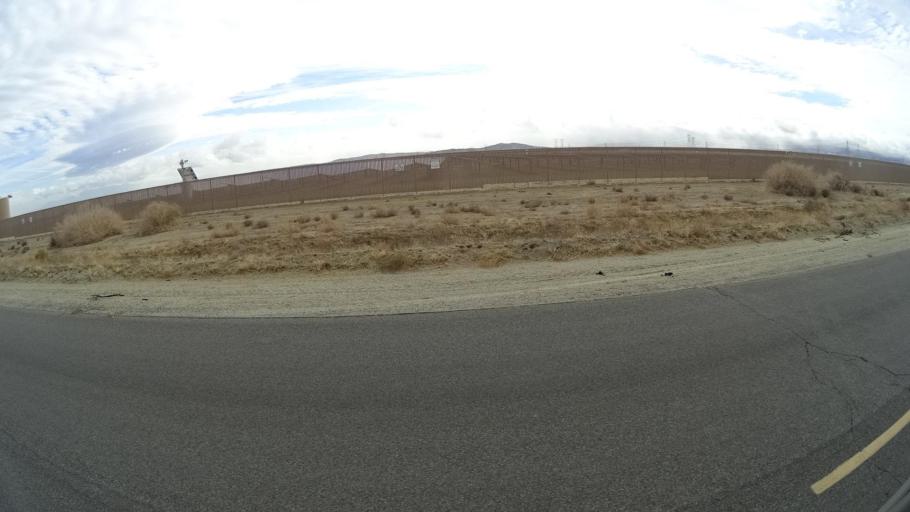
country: US
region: California
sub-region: Los Angeles County
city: Green Valley
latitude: 34.8192
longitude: -118.3945
